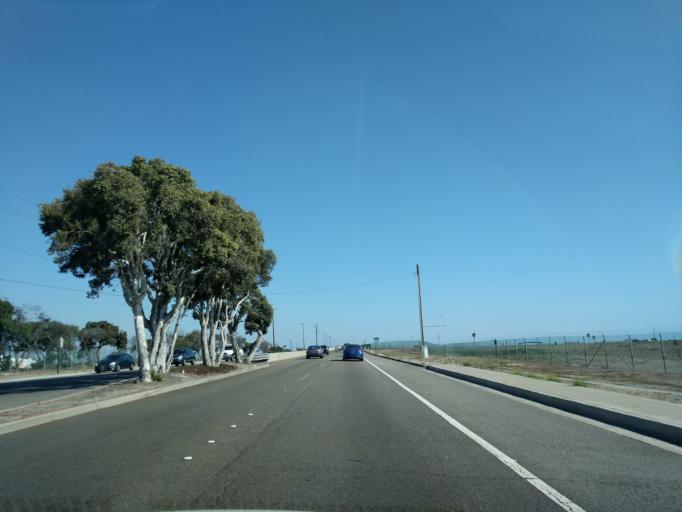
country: US
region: California
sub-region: Orange County
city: Seal Beach
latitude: 33.7405
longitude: -118.0950
